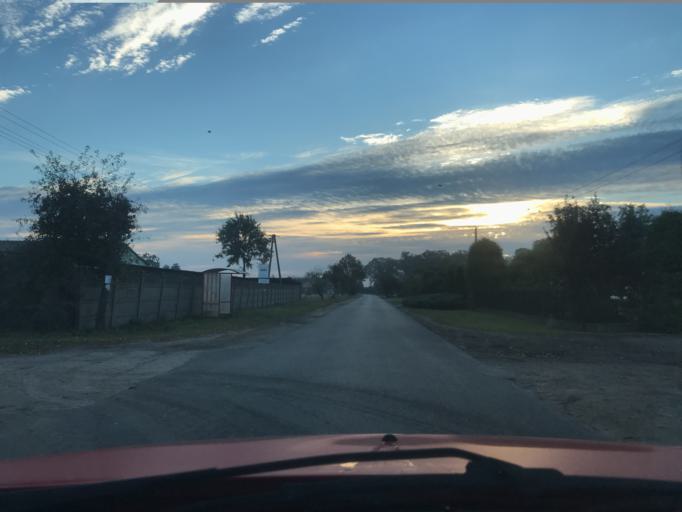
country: PL
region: Greater Poland Voivodeship
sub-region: Powiat ostrowski
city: Raszkow
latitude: 51.7192
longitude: 17.7878
